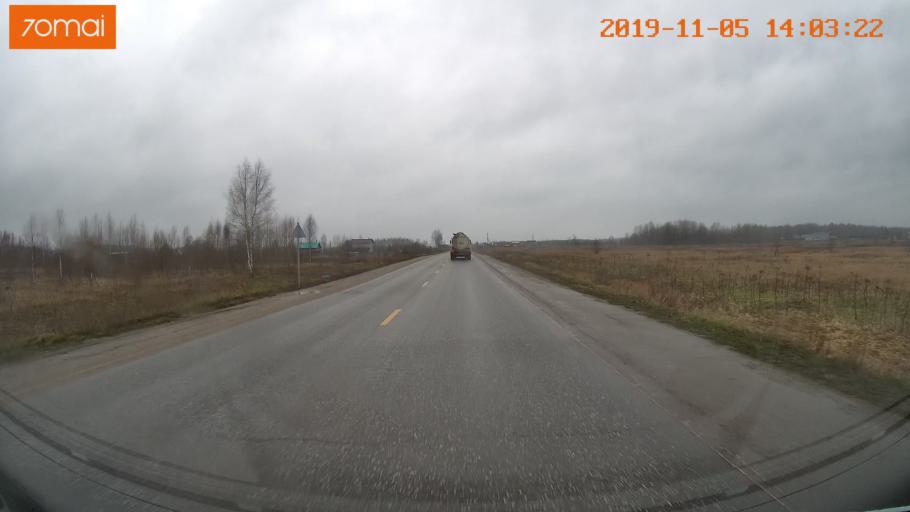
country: RU
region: Ivanovo
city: Kokhma
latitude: 56.9983
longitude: 41.1971
